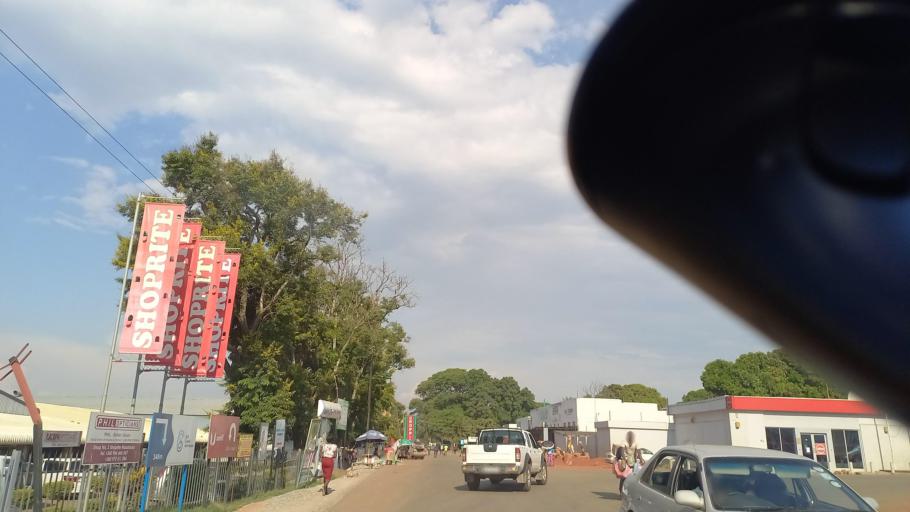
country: ZM
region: Southern
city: Mazabuka
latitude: -15.8580
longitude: 27.7631
